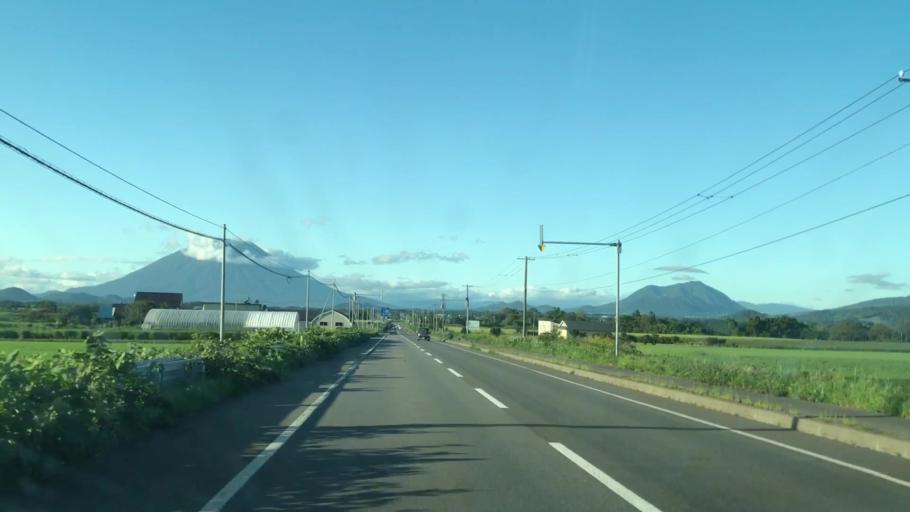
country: JP
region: Hokkaido
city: Date
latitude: 42.6376
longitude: 140.8021
